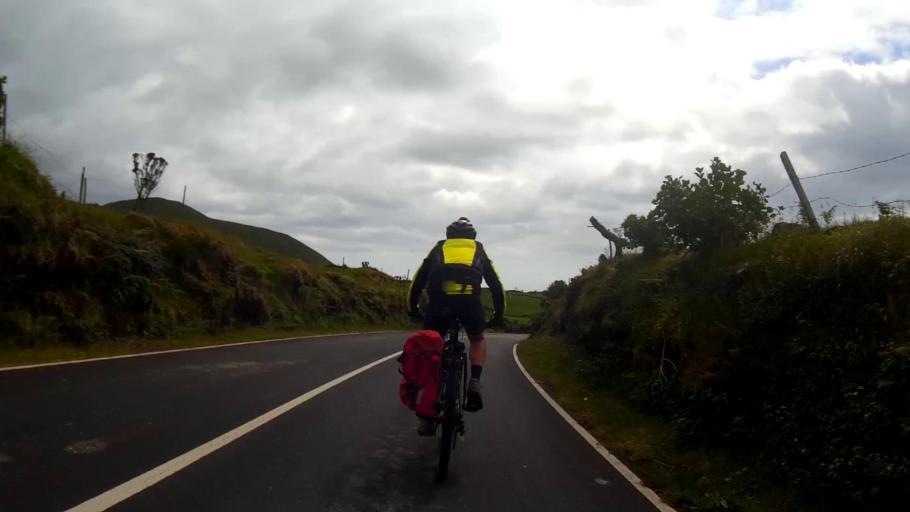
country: PT
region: Azores
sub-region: Madalena
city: Madalena
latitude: 38.4957
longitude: -28.4537
